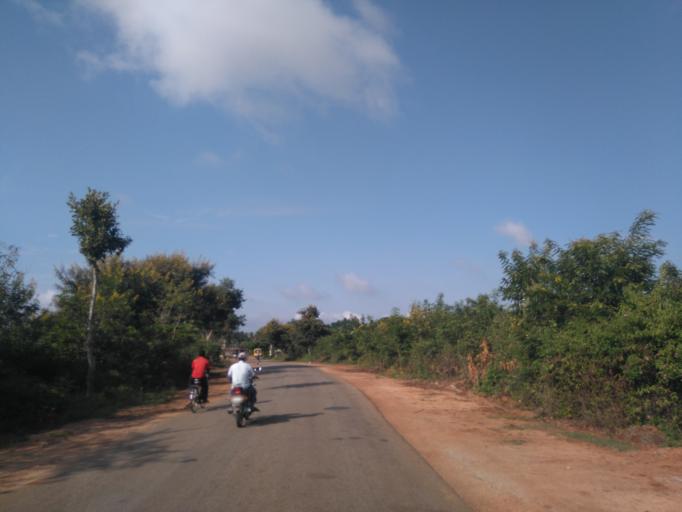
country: IN
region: Karnataka
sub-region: Mysore
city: Tirumakudal Narsipur
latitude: 12.2630
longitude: 77.0171
